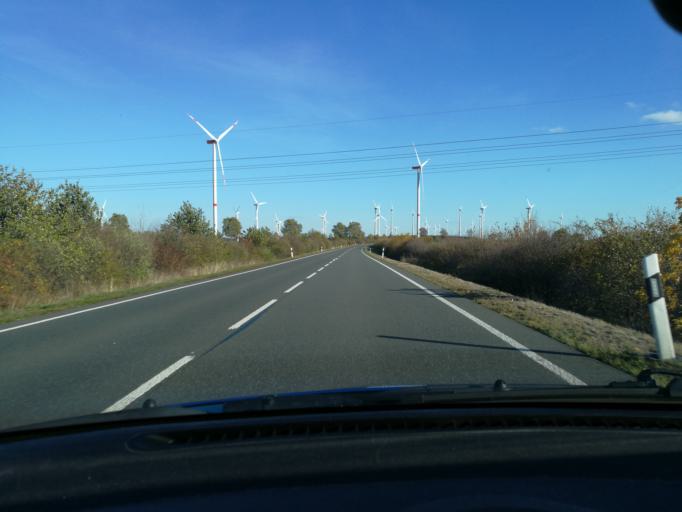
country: DE
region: Brandenburg
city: Karstadt
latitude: 53.1448
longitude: 11.7562
